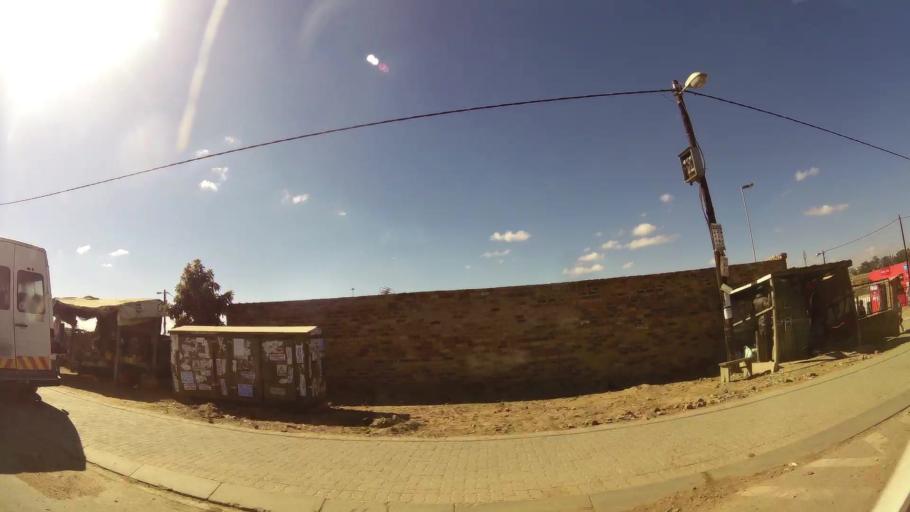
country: ZA
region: Gauteng
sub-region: City of Johannesburg Metropolitan Municipality
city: Midrand
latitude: -25.9230
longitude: 28.0919
